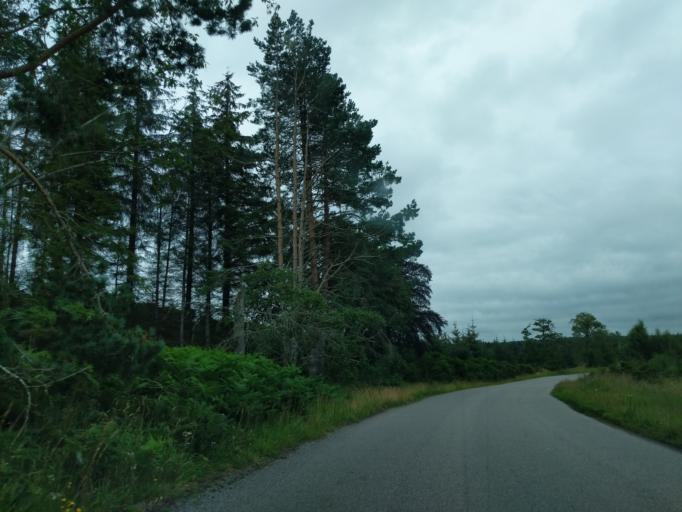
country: GB
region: Scotland
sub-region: Moray
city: Kinloss
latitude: 57.5539
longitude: -3.4883
